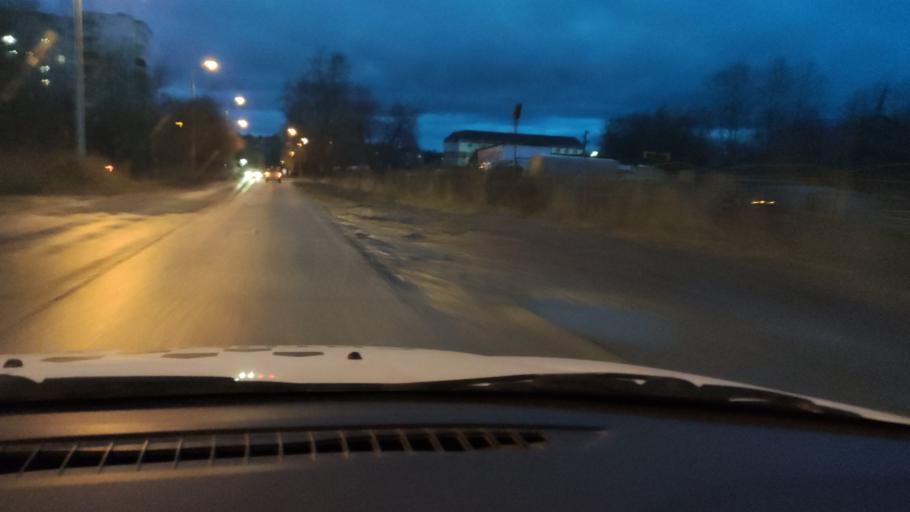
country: RU
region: Perm
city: Perm
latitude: 57.9755
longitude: 56.2794
